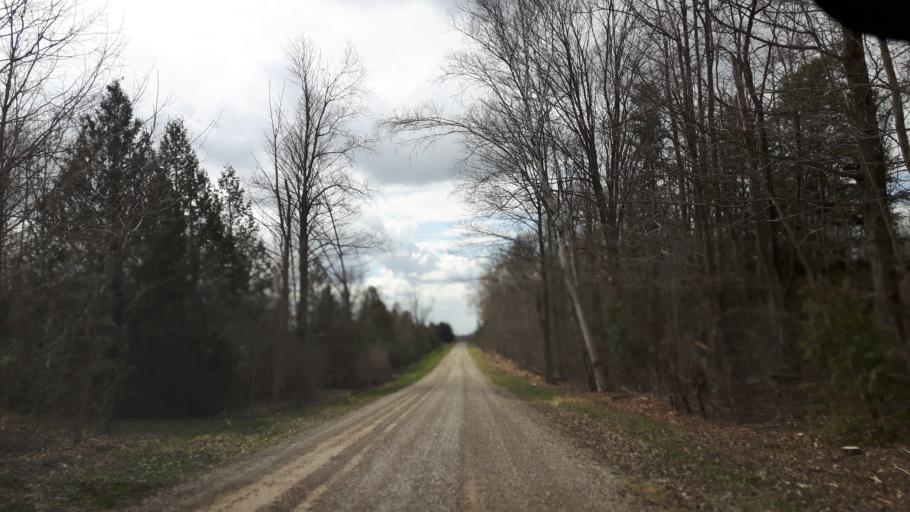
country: CA
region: Ontario
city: Bluewater
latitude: 43.5517
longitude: -81.6801
